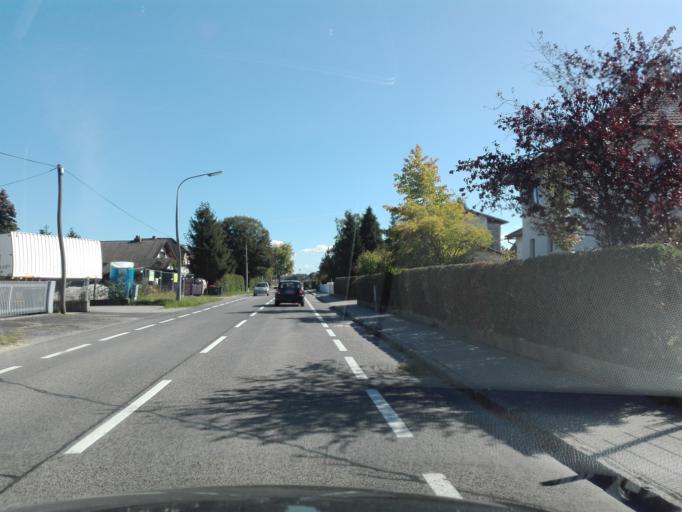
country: AT
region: Lower Austria
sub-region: Politischer Bezirk Amstetten
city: Ennsdorf
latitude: 48.2108
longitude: 14.4929
